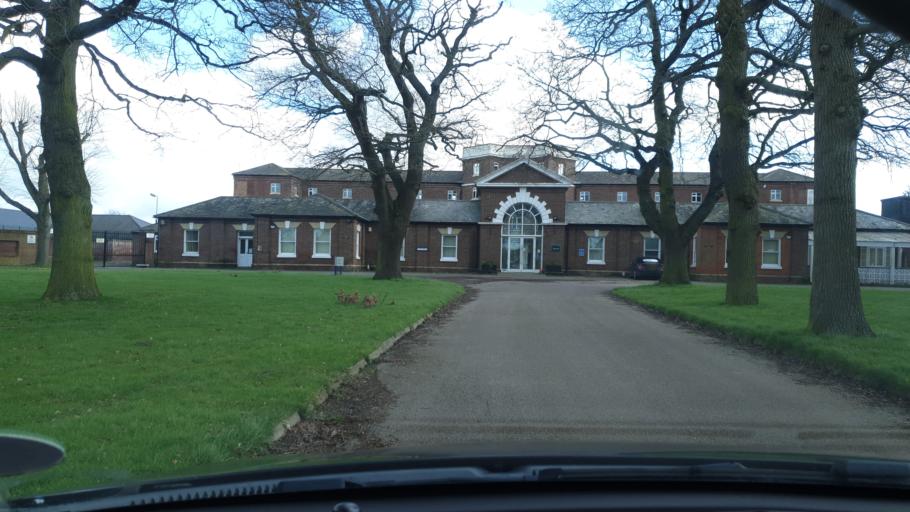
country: GB
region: England
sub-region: Essex
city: Mistley
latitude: 51.8958
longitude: 1.1002
